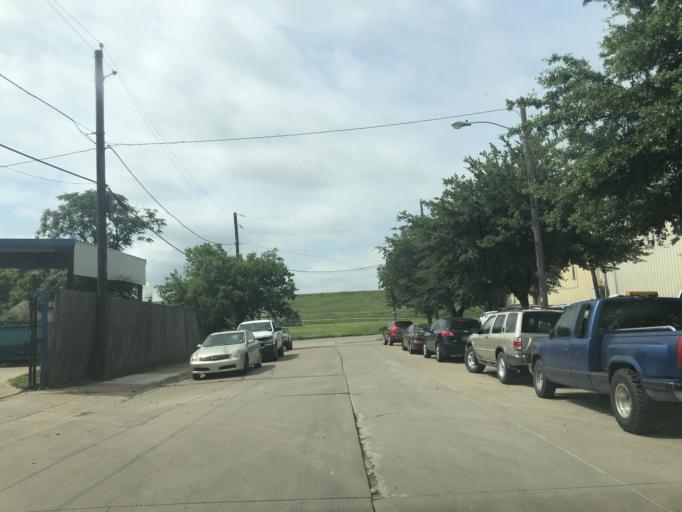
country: US
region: Texas
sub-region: Dallas County
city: Cockrell Hill
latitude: 32.8038
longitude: -96.8793
